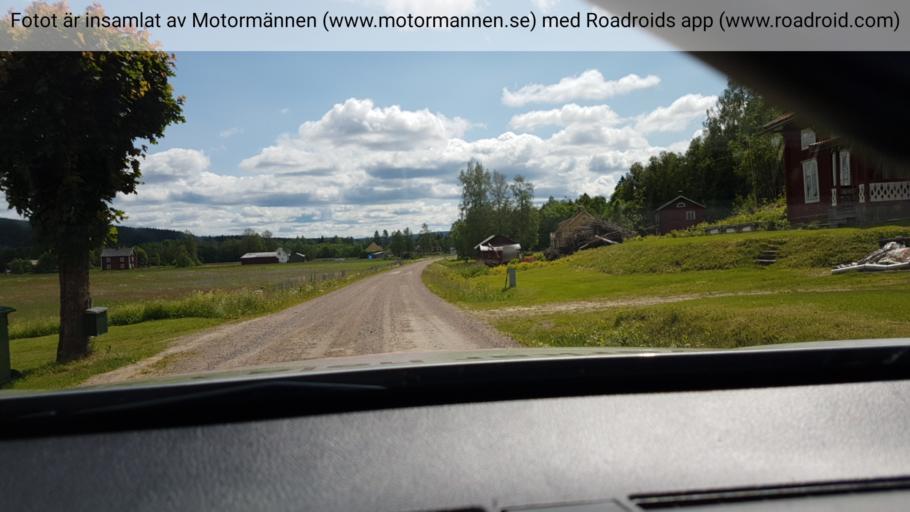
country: SE
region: Vaermland
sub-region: Hagfors Kommun
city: Ekshaerad
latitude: 60.3584
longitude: 13.3073
